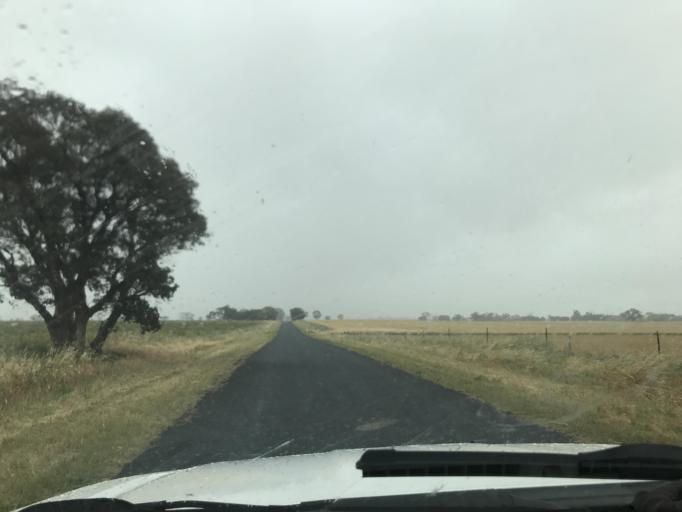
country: AU
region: South Australia
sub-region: Tatiara
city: Bordertown
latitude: -36.3165
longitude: 141.1768
